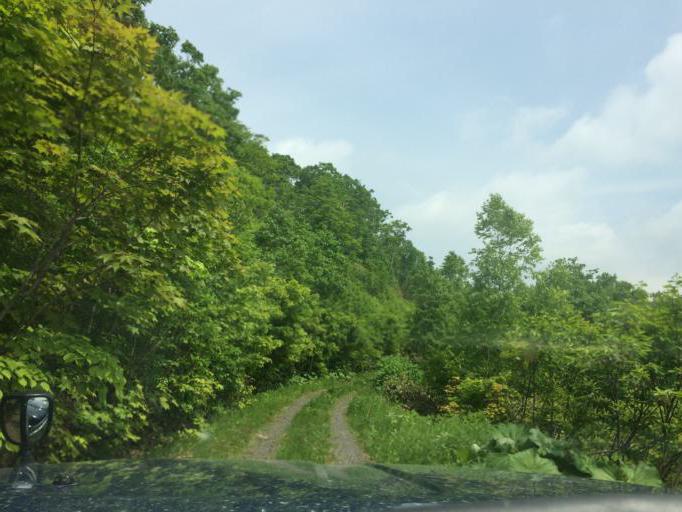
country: JP
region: Hokkaido
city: Niseko Town
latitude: 42.6820
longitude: 140.6145
